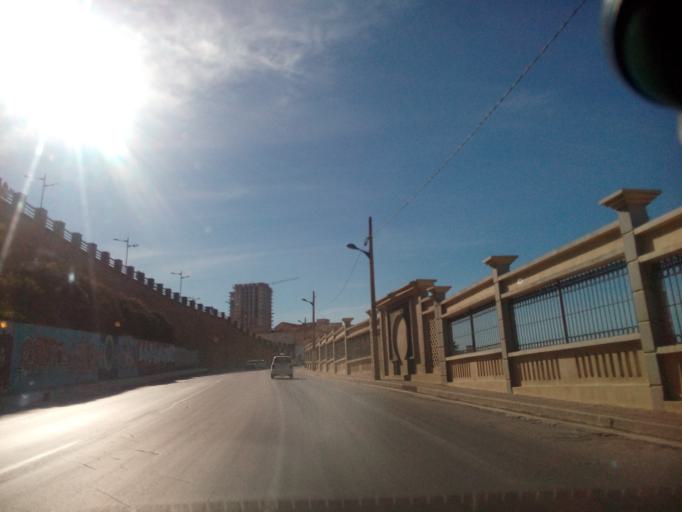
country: DZ
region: Mostaganem
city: Mostaganem
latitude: 35.9272
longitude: 0.0767
